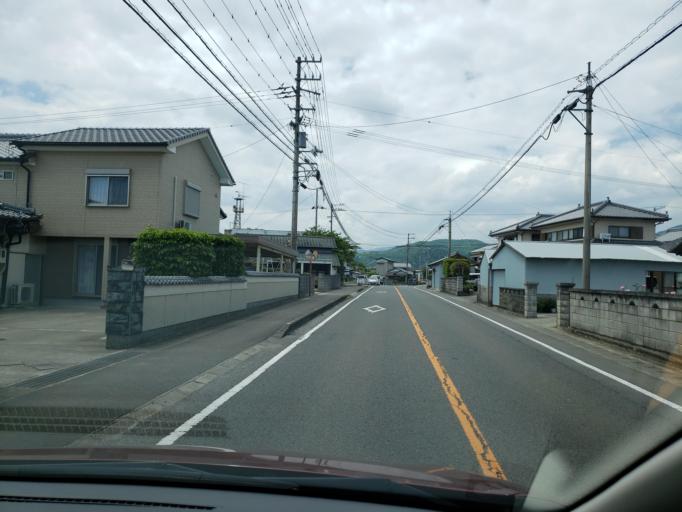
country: JP
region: Tokushima
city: Kamojimacho-jogejima
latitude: 34.0978
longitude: 134.3391
